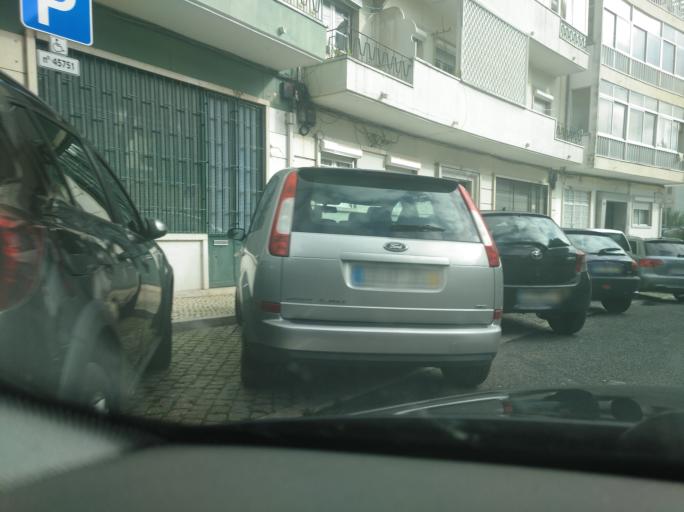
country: PT
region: Lisbon
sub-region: Odivelas
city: Pontinha
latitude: 38.7462
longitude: -9.1777
